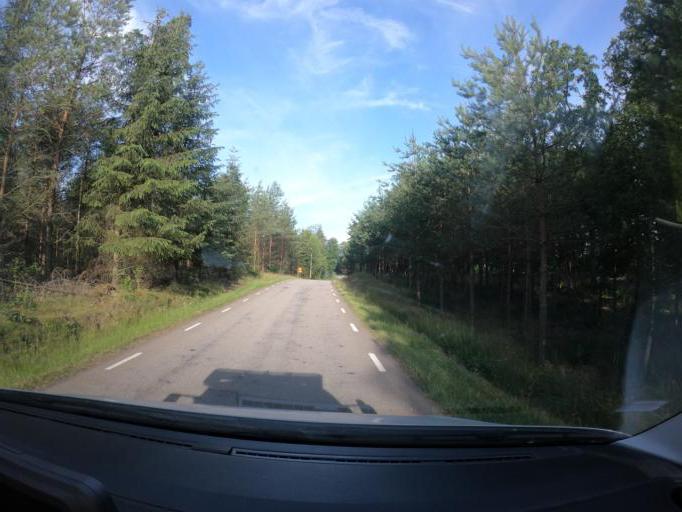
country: SE
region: Skane
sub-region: Angelholms Kommun
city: Munka-Ljungby
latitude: 56.3113
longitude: 13.0562
